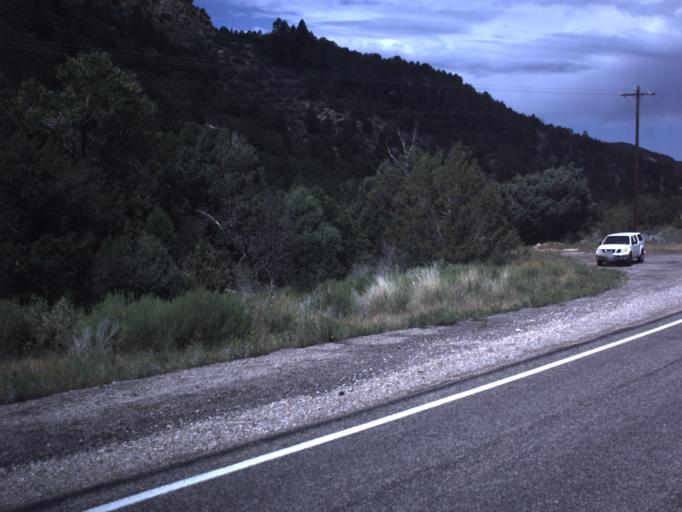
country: US
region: Utah
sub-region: Iron County
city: Cedar City
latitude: 37.6459
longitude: -112.9680
